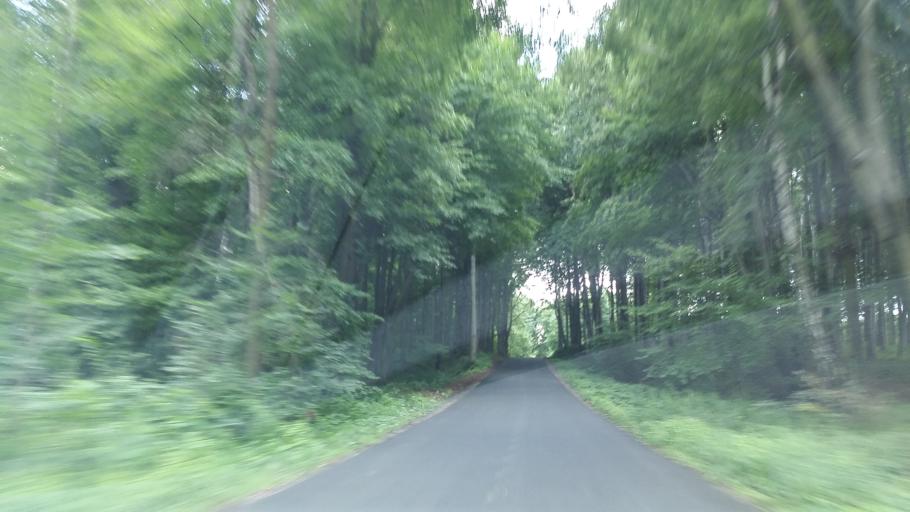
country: PL
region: Lesser Poland Voivodeship
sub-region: Powiat wadowicki
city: Bachowice
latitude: 49.9813
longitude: 19.4760
